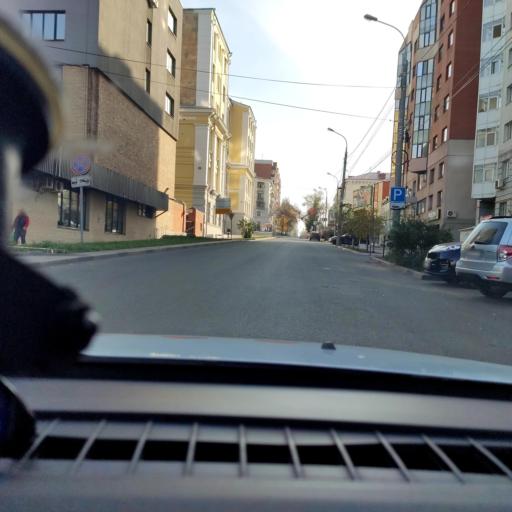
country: RU
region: Samara
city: Samara
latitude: 53.2004
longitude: 50.1033
